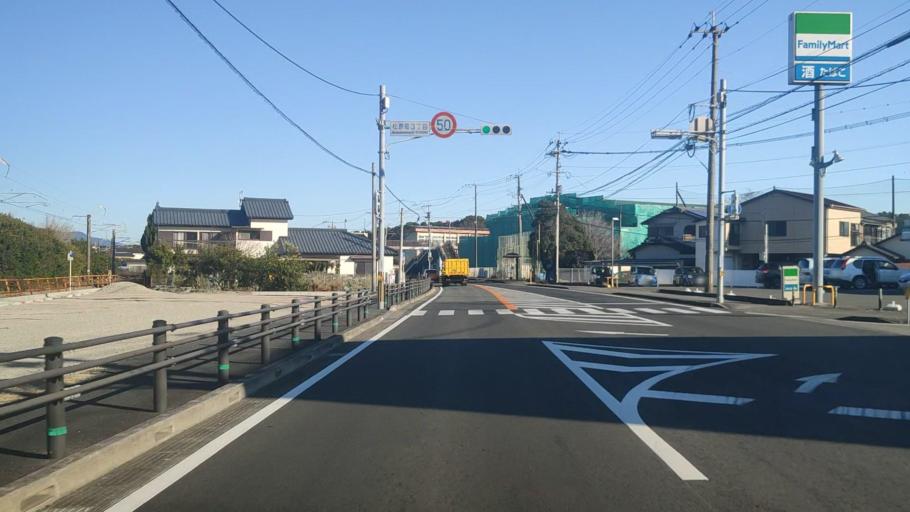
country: JP
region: Miyazaki
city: Nobeoka
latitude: 32.5197
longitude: 131.6831
